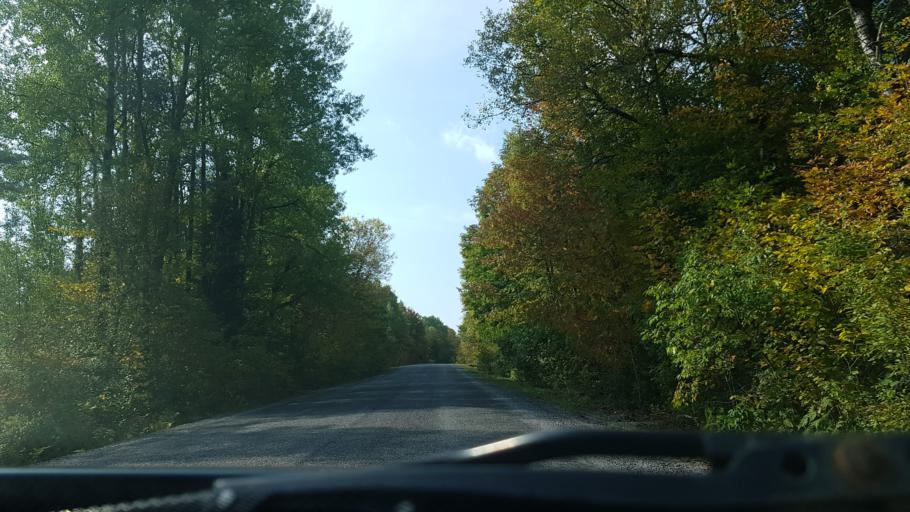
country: CA
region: Ontario
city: Gravenhurst
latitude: 44.8372
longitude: -79.2139
